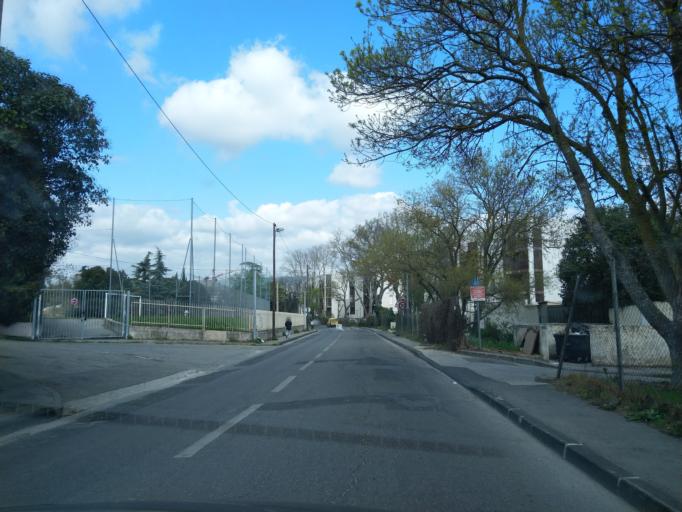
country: FR
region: Provence-Alpes-Cote d'Azur
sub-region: Departement des Bouches-du-Rhone
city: Plan-de-Cuques
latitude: 43.3308
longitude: 5.4576
